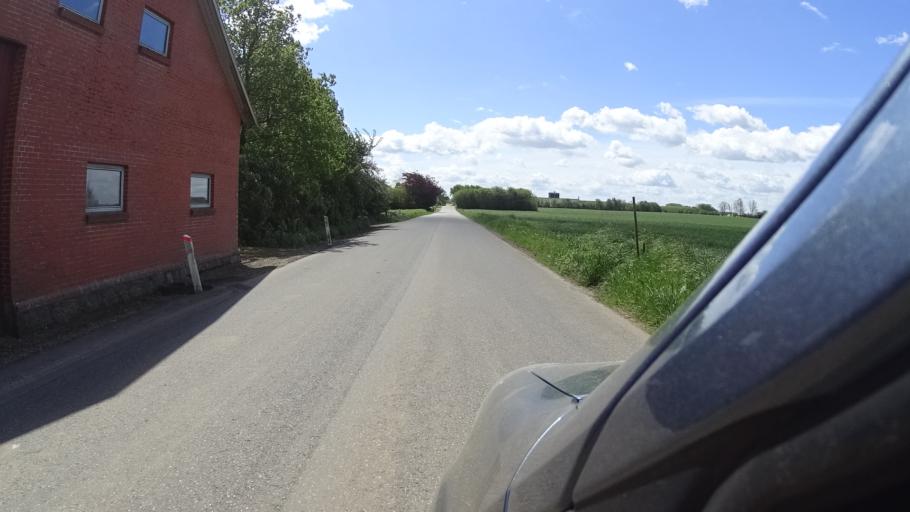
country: DK
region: South Denmark
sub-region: Fredericia Kommune
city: Taulov
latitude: 55.6029
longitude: 9.5590
